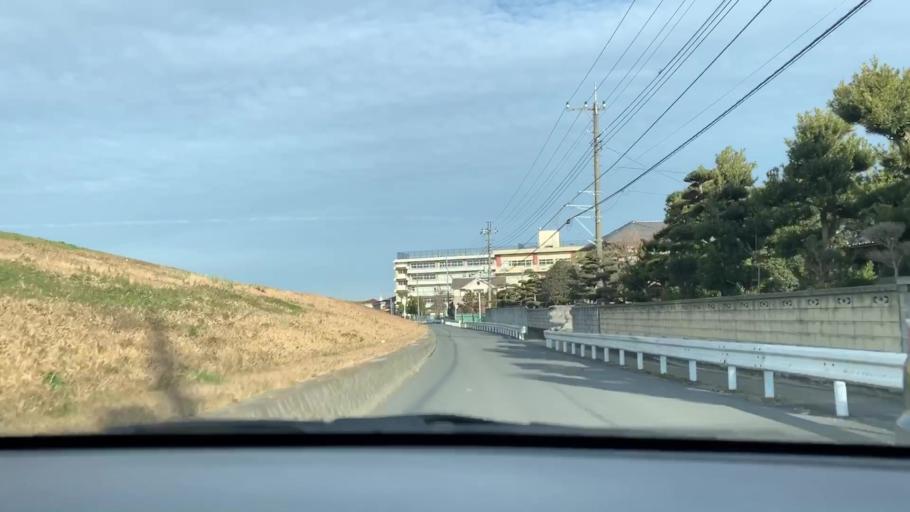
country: JP
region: Chiba
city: Matsudo
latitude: 35.8030
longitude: 139.8943
